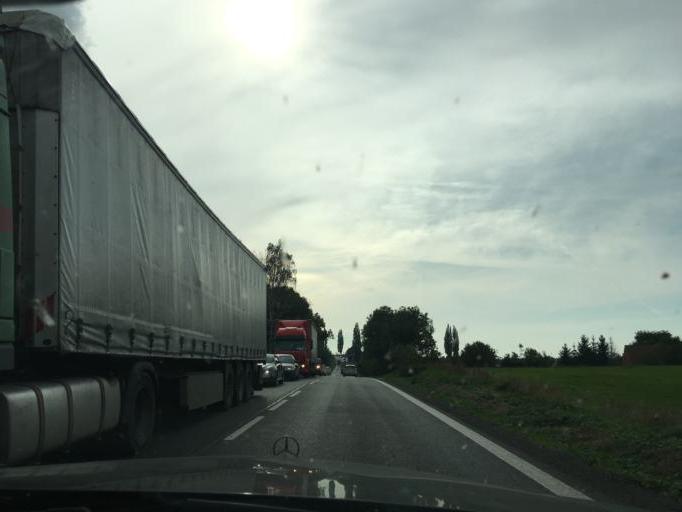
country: CZ
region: Kralovehradecky
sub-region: Okres Hradec Kralove
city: Smirice
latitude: 50.2901
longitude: 15.8321
